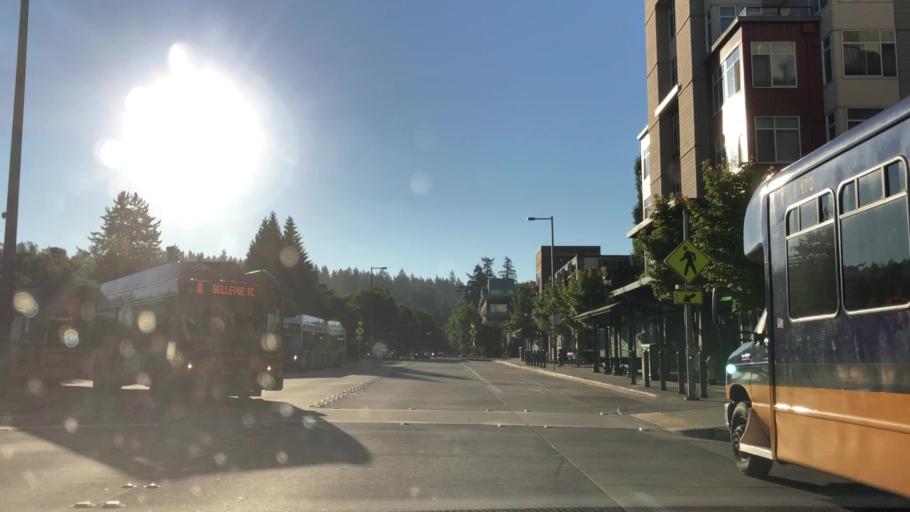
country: US
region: Washington
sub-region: King County
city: Redmond
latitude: 47.6766
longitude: -122.1248
